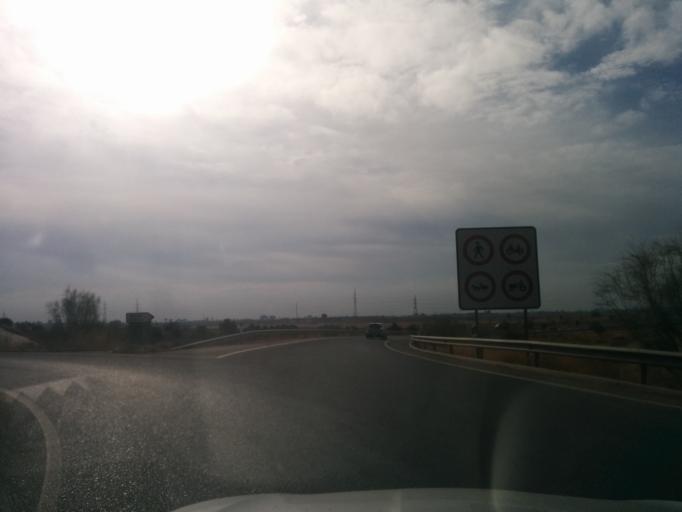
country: ES
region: Andalusia
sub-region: Provincia de Sevilla
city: La Rinconada
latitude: 37.4541
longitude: -5.9718
